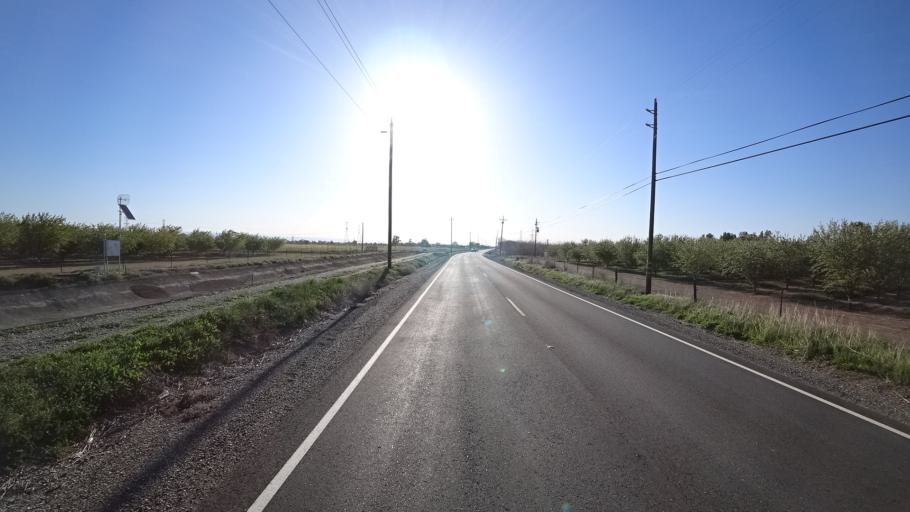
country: US
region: California
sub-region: Glenn County
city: Orland
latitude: 39.7782
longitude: -122.2817
